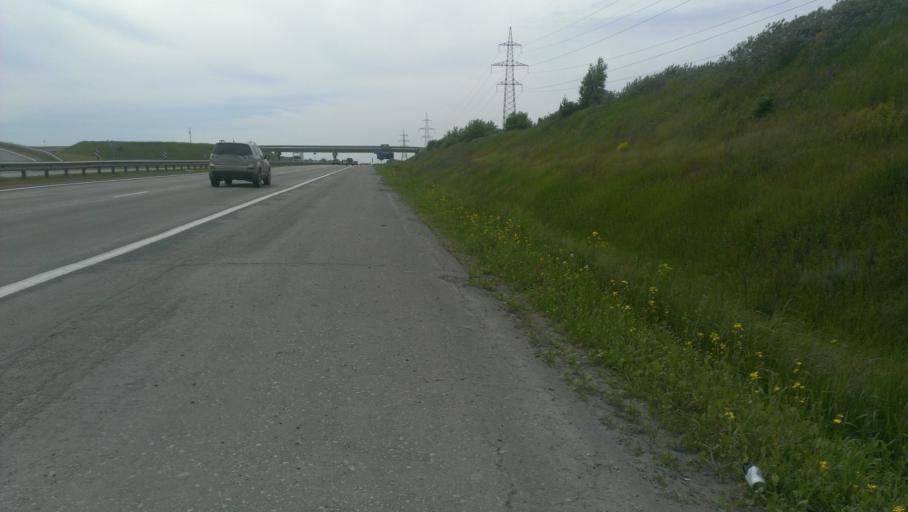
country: RU
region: Altai Krai
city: Sannikovo
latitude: 53.3430
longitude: 83.9393
